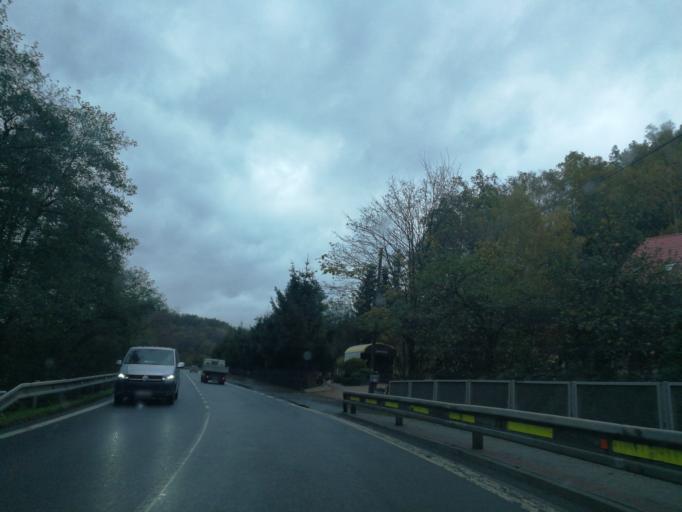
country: CZ
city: Hodslavice
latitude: 49.5286
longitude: 18.0179
